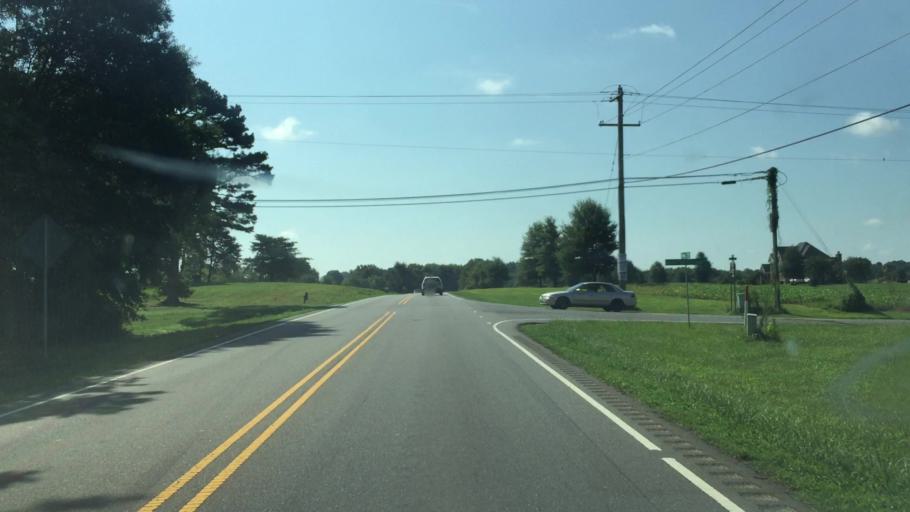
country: US
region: North Carolina
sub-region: Union County
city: Fairview
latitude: 35.1423
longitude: -80.5471
